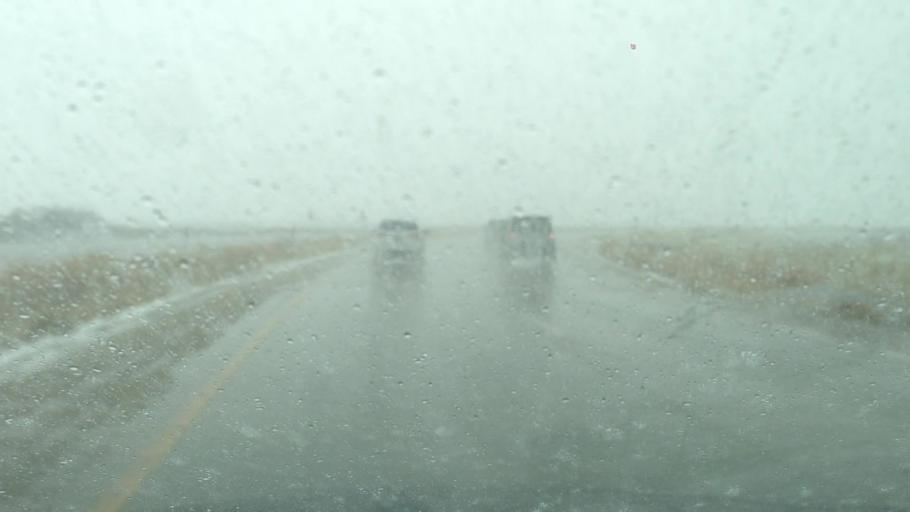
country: US
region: Colorado
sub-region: Park County
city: Castle Pines North
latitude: 39.4708
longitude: -104.8652
